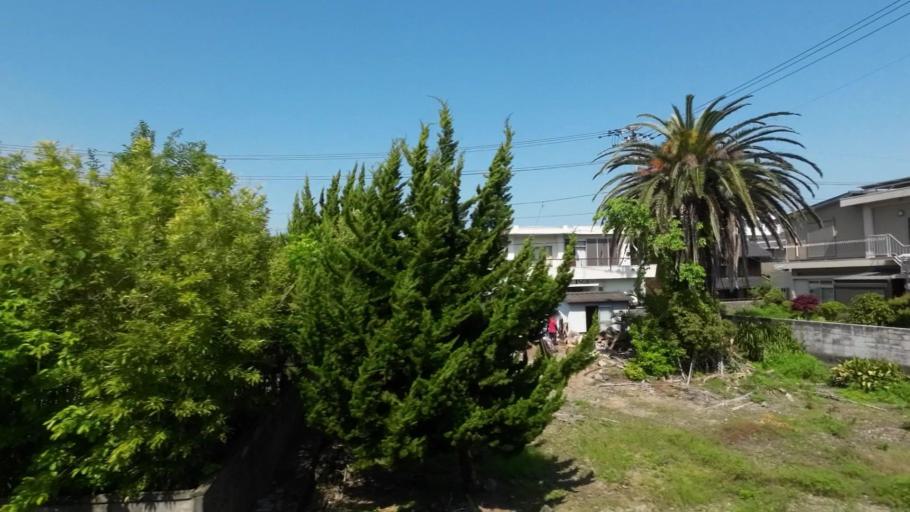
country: JP
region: Ehime
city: Kawanoecho
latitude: 34.0190
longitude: 133.5771
